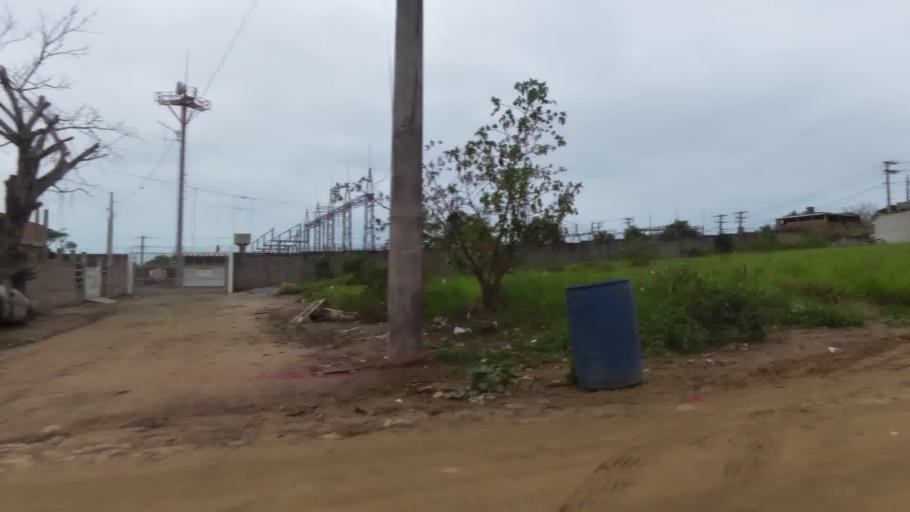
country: BR
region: Espirito Santo
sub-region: Marataizes
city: Marataizes
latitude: -21.0405
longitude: -40.8360
